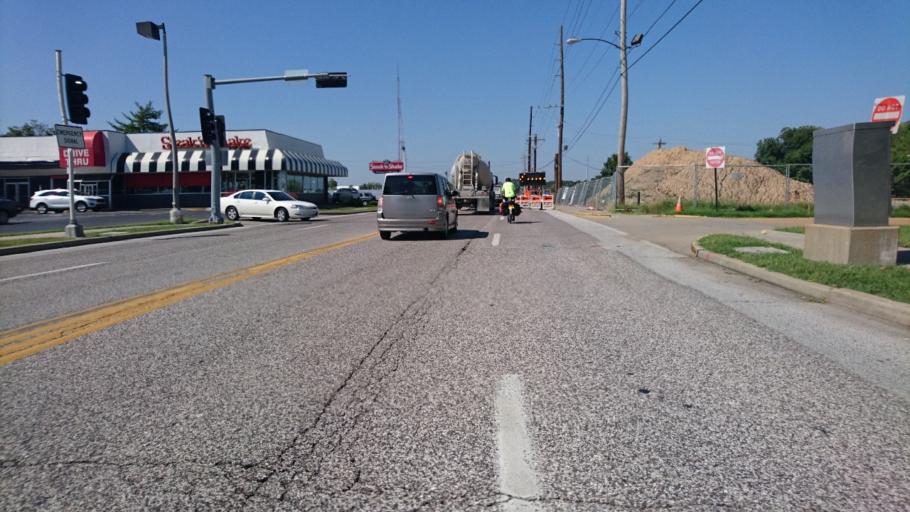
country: US
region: Missouri
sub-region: Saint Louis County
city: Maplewood
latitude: 38.6129
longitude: -90.3261
